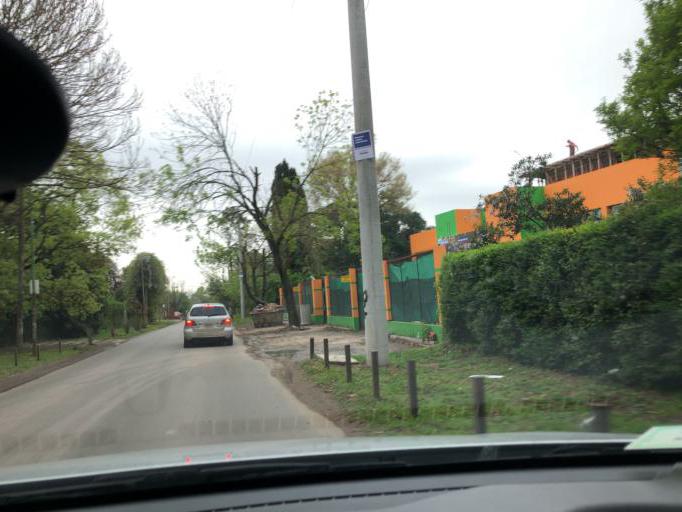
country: AR
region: Buenos Aires
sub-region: Partido de La Plata
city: La Plata
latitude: -34.8922
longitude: -58.0645
